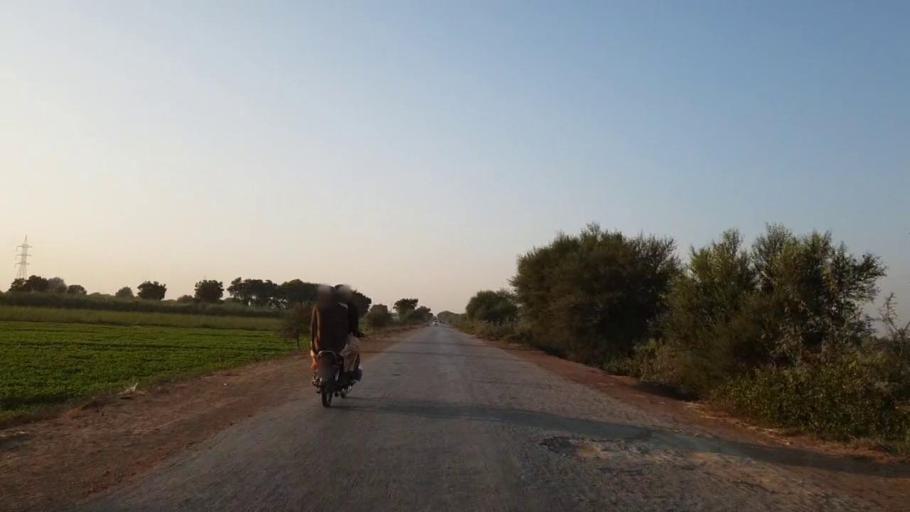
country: PK
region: Sindh
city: Chambar
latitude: 25.2359
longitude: 68.6986
